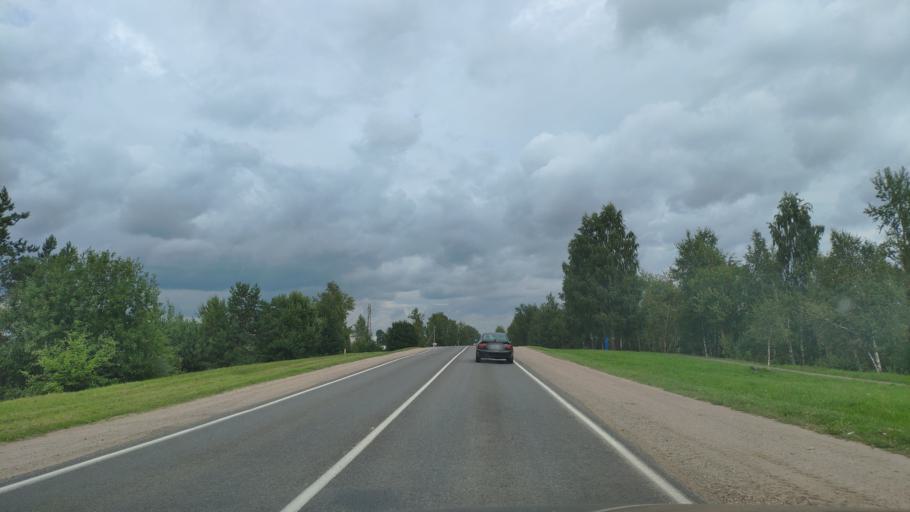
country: BY
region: Minsk
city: Zaslawye
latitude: 53.9907
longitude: 27.2635
